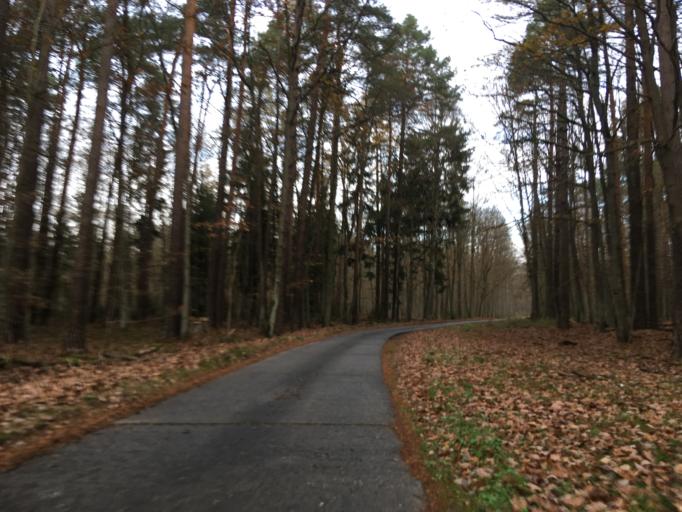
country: DE
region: Brandenburg
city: Tauer
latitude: 51.9518
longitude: 14.5180
